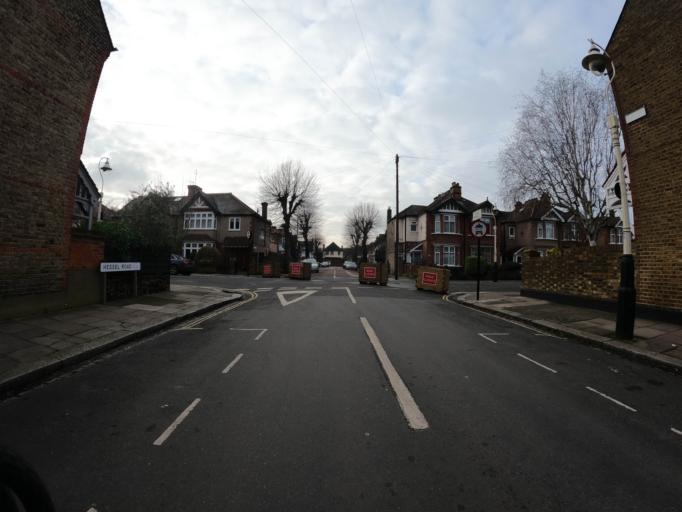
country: GB
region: England
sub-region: Greater London
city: Ealing
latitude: 51.5039
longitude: -0.3245
